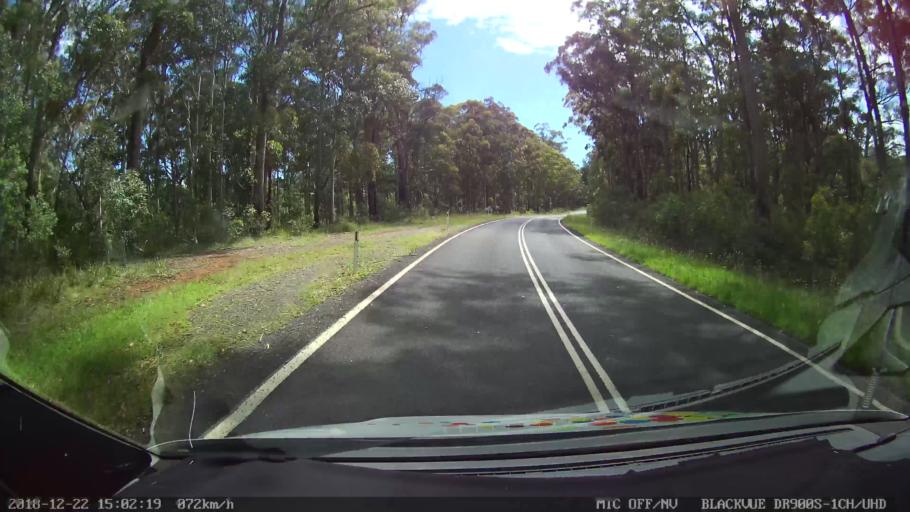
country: AU
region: New South Wales
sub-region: Bellingen
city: Dorrigo
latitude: -30.2609
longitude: 152.4519
